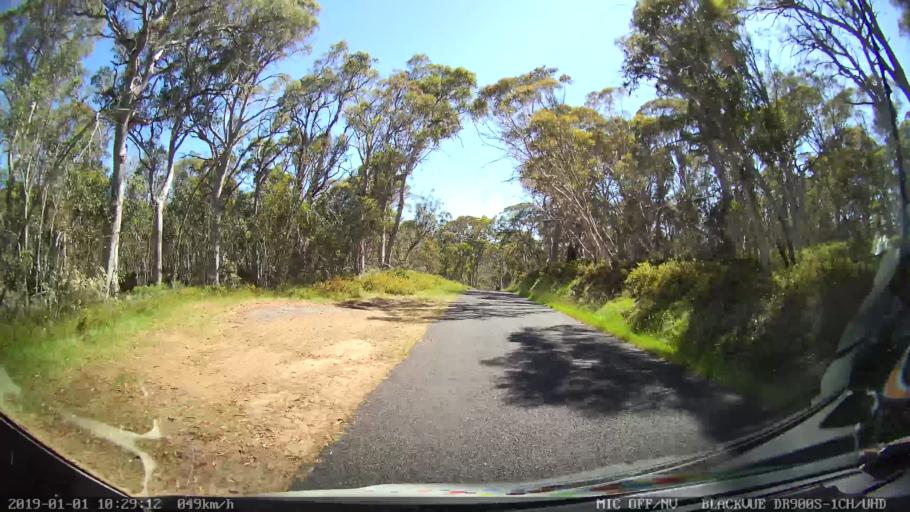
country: AU
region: New South Wales
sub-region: Snowy River
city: Jindabyne
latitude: -36.0558
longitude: 148.2460
